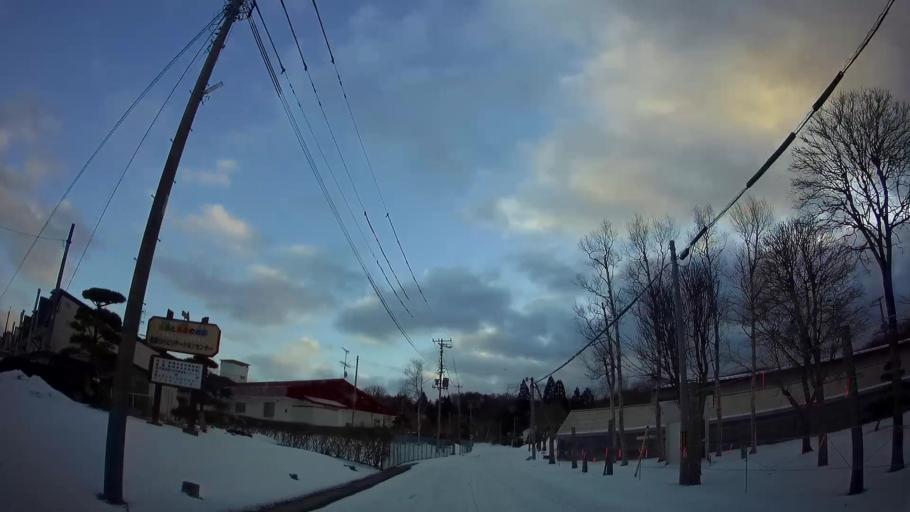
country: JP
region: Hokkaido
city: Nanae
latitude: 42.0242
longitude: 140.8329
